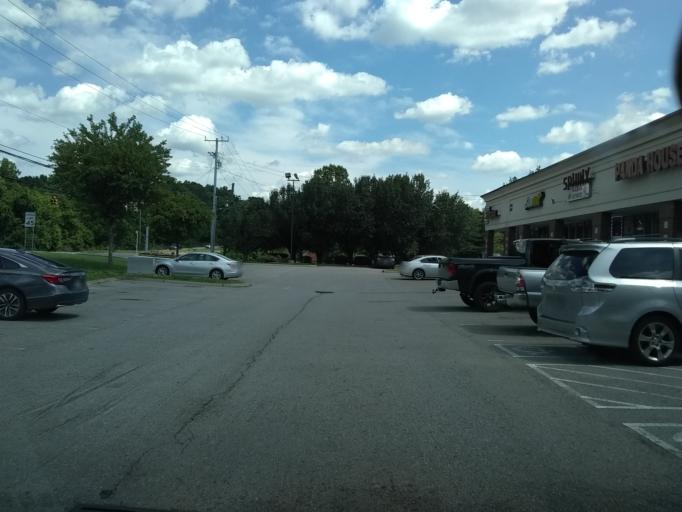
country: US
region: Tennessee
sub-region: Davidson County
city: Nashville
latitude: 36.1364
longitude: -86.6997
